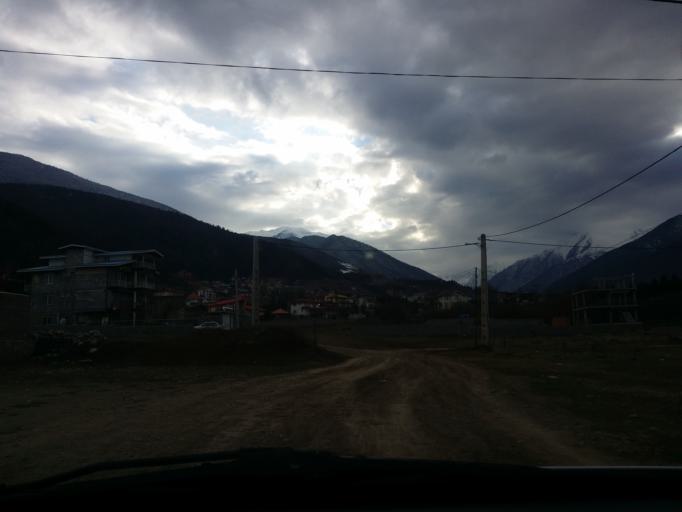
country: IR
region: Mazandaran
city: `Abbasabad
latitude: 36.5012
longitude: 51.1725
